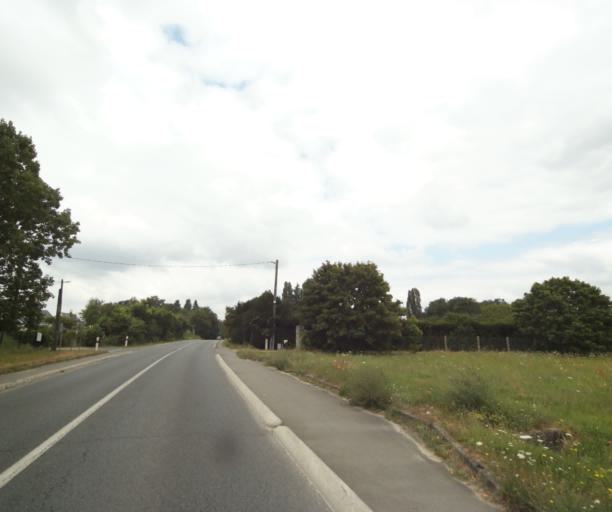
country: FR
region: Centre
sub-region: Departement du Loiret
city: Saint-Jean-de-Braye
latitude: 47.9032
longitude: 1.9969
